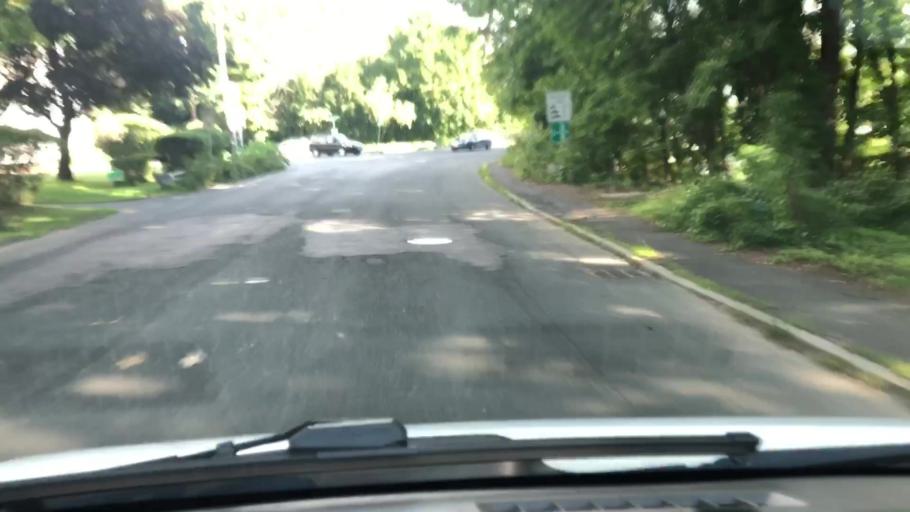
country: US
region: Massachusetts
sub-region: Franklin County
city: Greenfield
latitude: 42.5790
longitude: -72.5801
